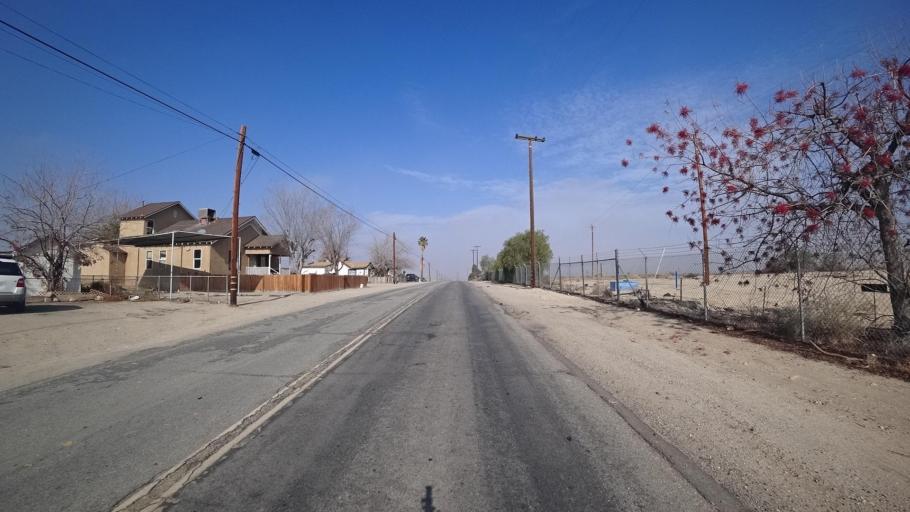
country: US
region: California
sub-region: Kern County
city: Ford City
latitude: 35.1682
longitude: -119.4653
